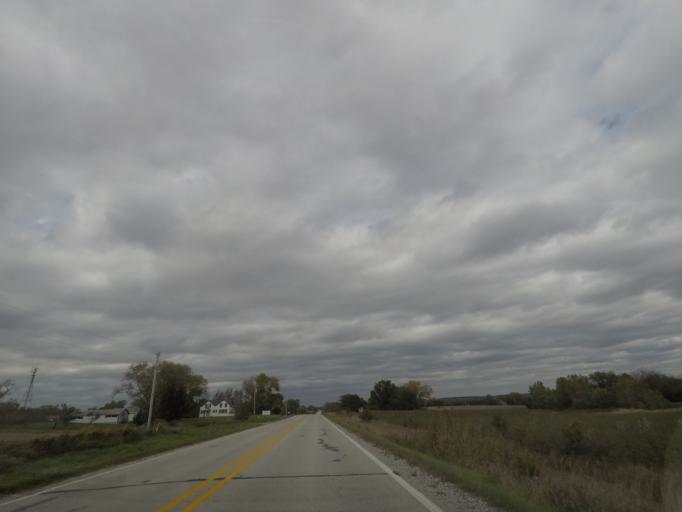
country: US
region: Iowa
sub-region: Story County
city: Huxley
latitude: 41.8607
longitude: -93.5316
